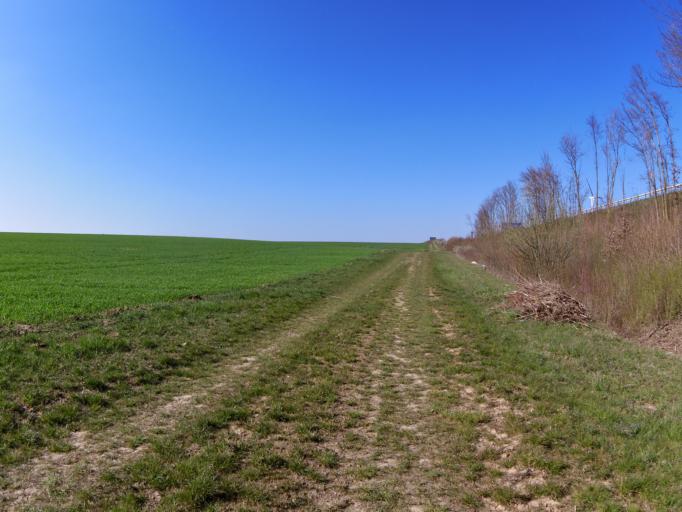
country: DE
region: Bavaria
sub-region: Regierungsbezirk Unterfranken
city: Biebelried
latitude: 49.7627
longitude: 10.1036
